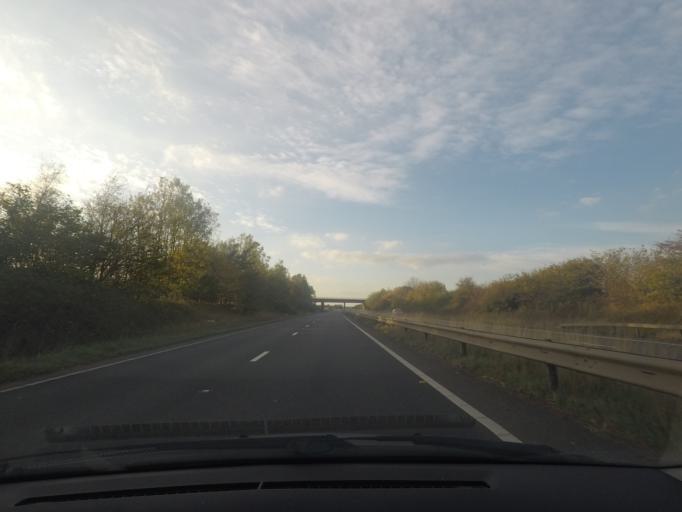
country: GB
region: England
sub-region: North East Lincolnshire
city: Immingham
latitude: 53.6020
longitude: -0.2160
